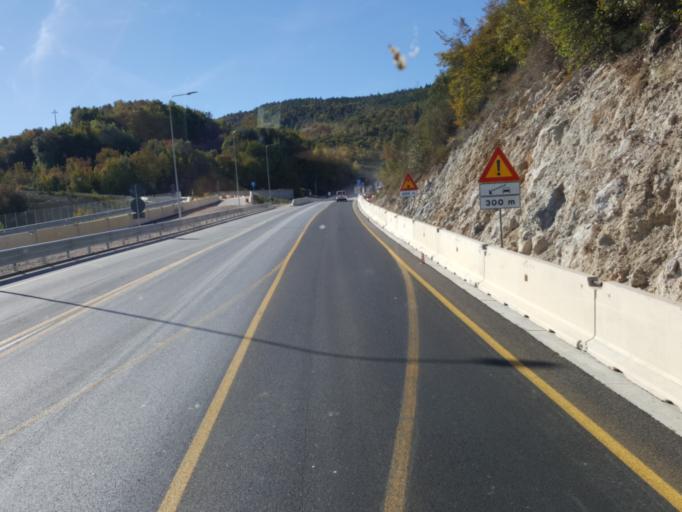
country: IT
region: Tuscany
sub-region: Provincia di Grosseto
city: Civitella Marittima
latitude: 43.0697
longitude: 11.2961
